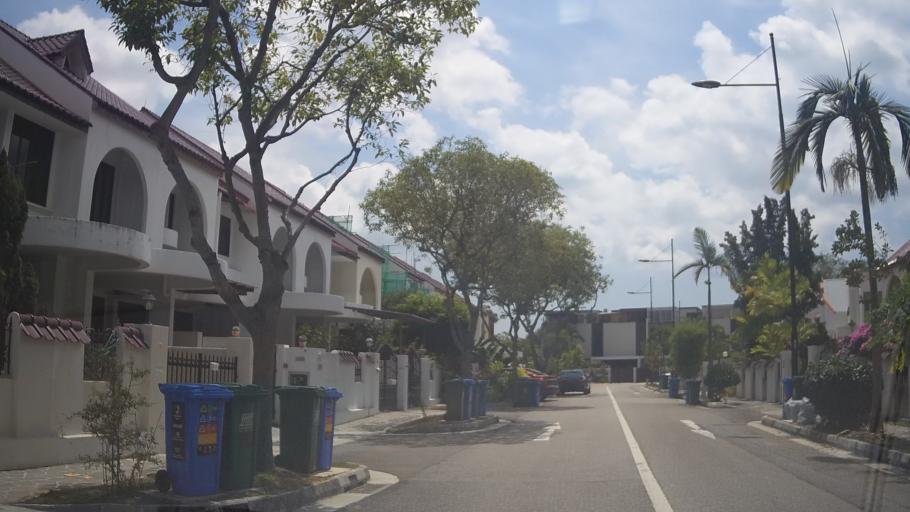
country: SG
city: Singapore
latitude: 1.3271
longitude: 103.9516
